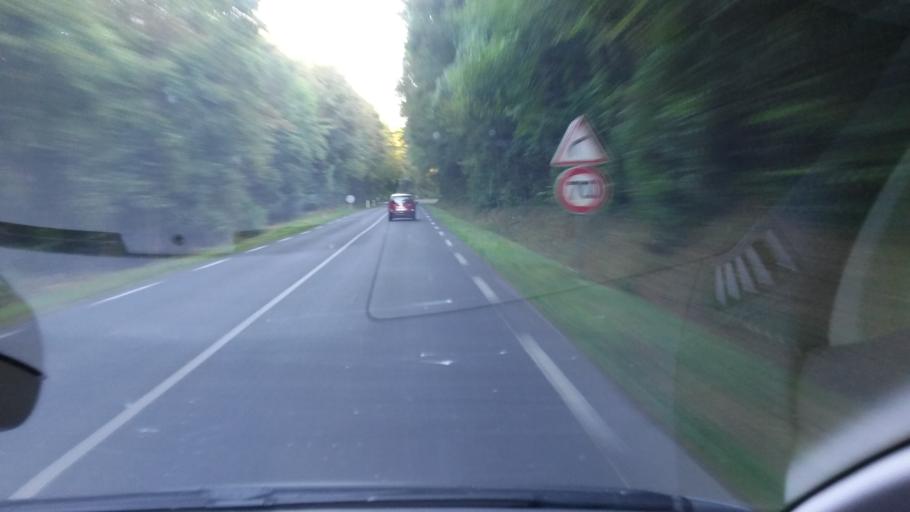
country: FR
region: Champagne-Ardenne
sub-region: Departement de la Marne
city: Verzenay
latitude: 49.1392
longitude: 4.1049
